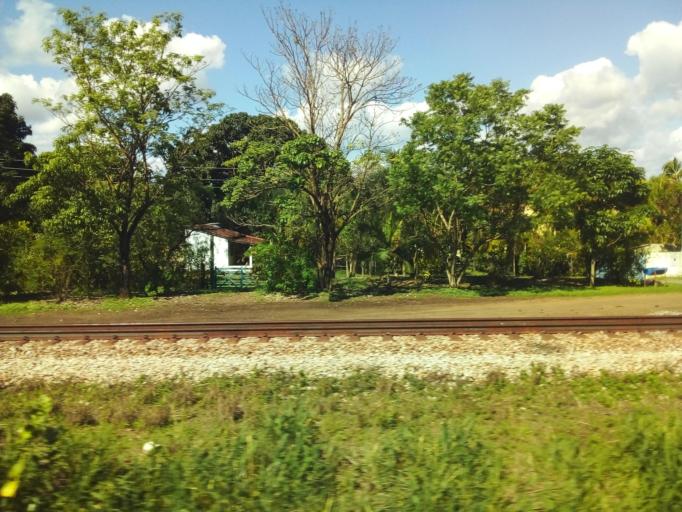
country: BR
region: Minas Gerais
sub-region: Governador Valadares
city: Governador Valadares
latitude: -18.8598
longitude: -41.8628
